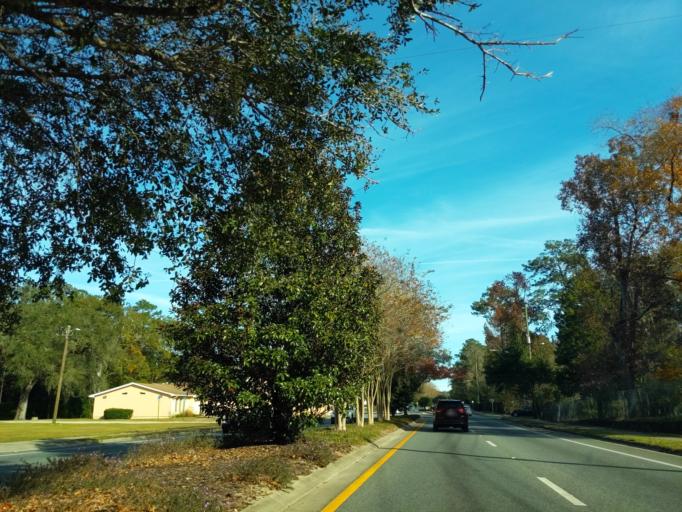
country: US
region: Florida
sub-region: Leon County
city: Tallahassee
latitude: 30.4126
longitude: -84.2753
